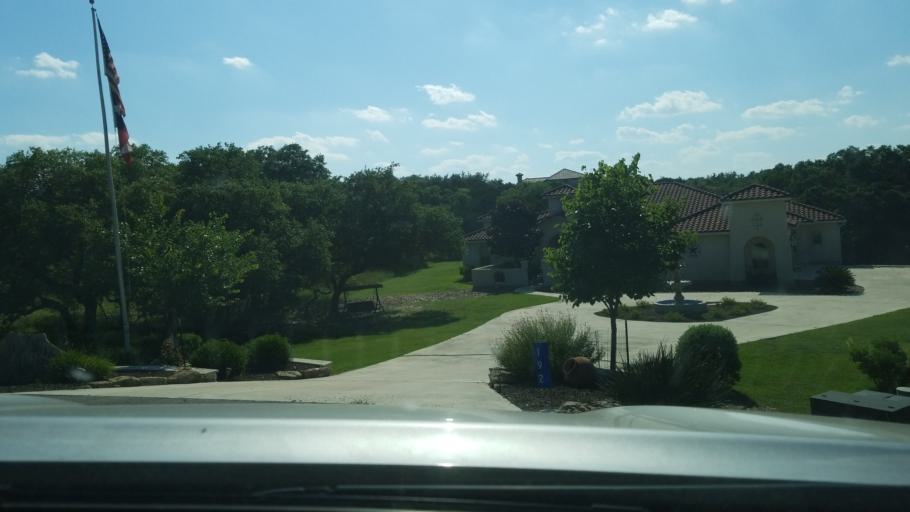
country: US
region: Texas
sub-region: Comal County
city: Bulverde
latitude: 29.8284
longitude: -98.4044
